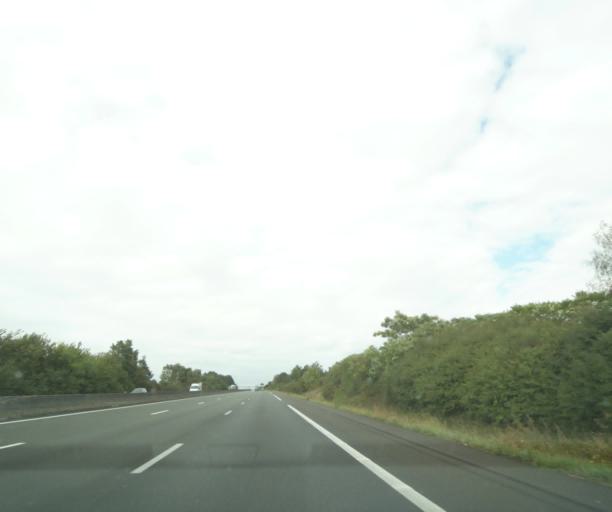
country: FR
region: Centre
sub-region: Departement d'Eure-et-Loir
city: Janville
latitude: 48.2347
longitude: 1.8499
